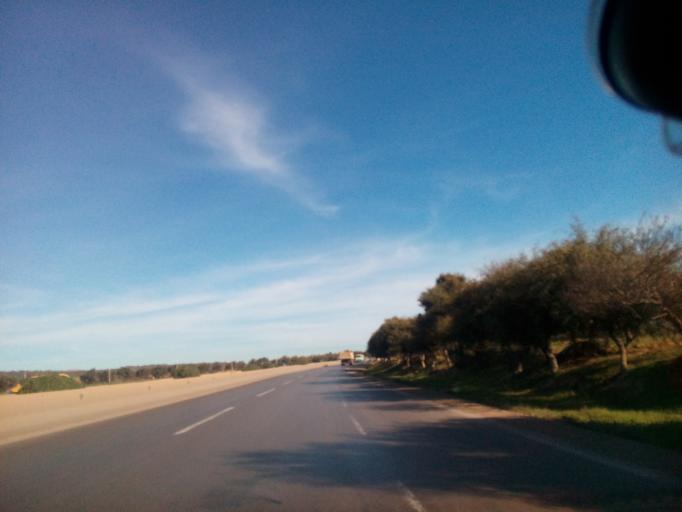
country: DZ
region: Oran
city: Ain el Bya
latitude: 35.7864
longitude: -0.4106
